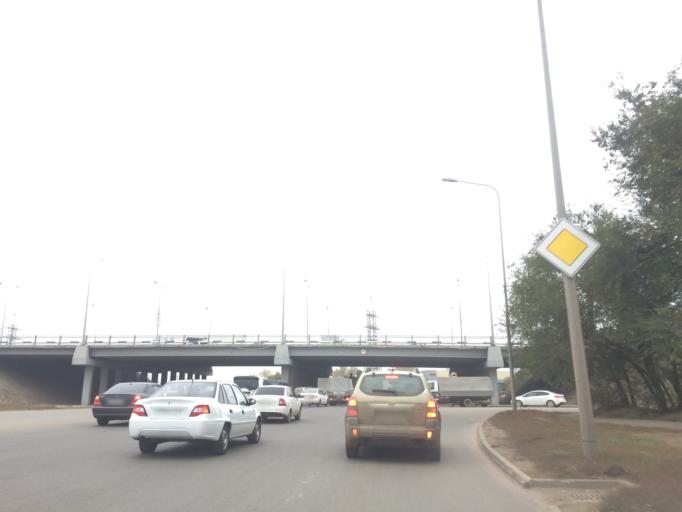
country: KZ
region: Astana Qalasy
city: Astana
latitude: 51.1854
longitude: 71.4490
